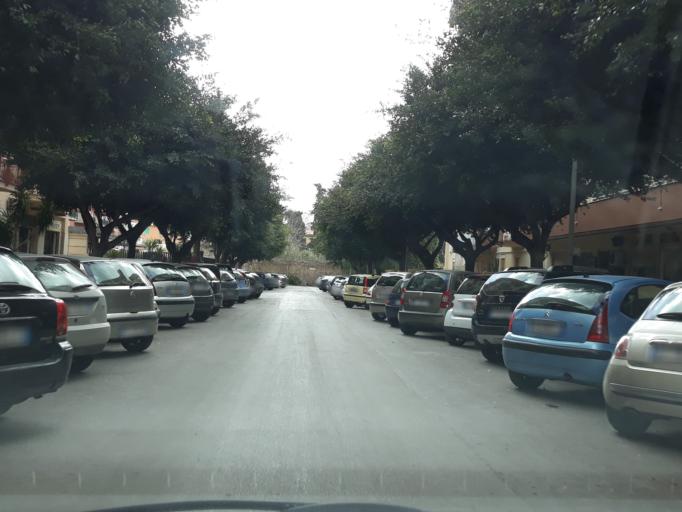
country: IT
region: Sicily
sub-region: Palermo
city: Palermo
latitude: 38.1142
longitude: 13.3406
